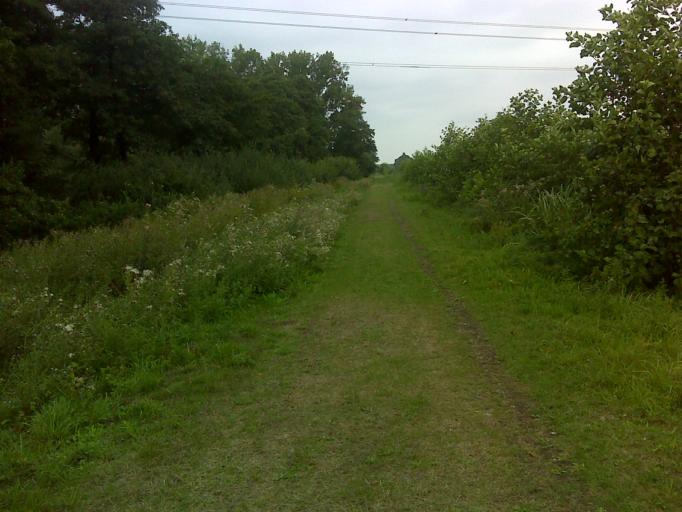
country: FR
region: Nord-Pas-de-Calais
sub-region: Departement du Nord
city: Landrecies
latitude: 50.1173
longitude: 3.6746
